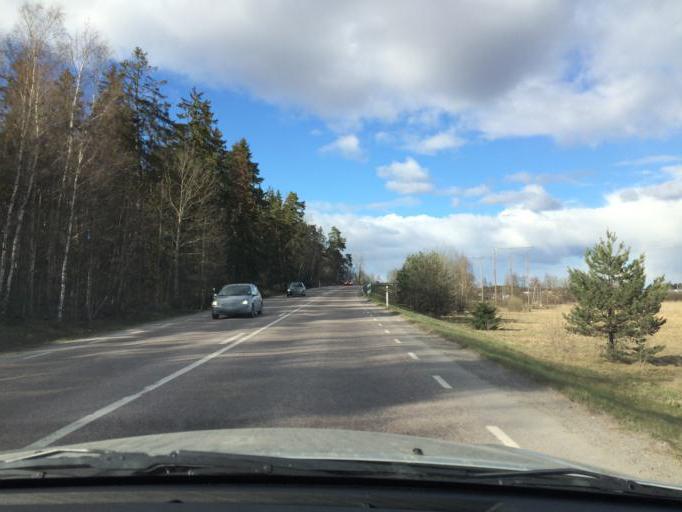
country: SE
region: Soedermanland
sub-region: Eskilstuna Kommun
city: Torshalla
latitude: 59.3816
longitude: 16.4611
